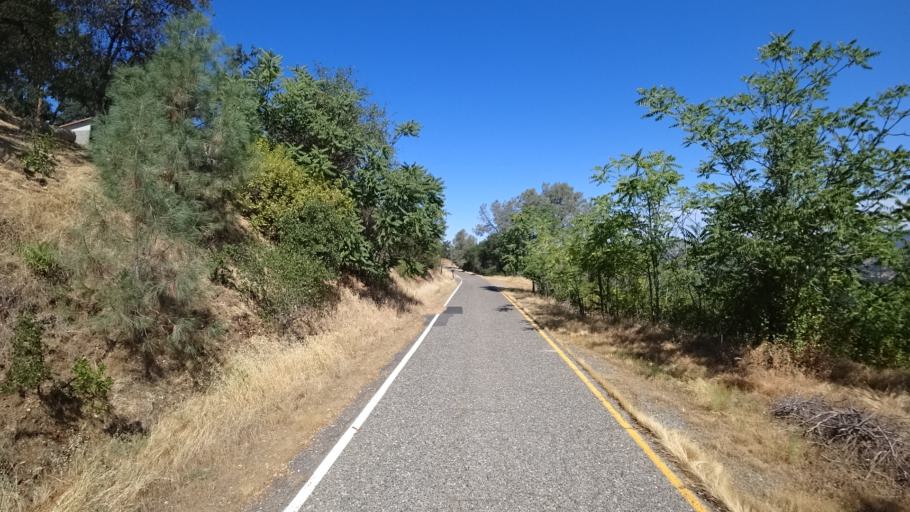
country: US
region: California
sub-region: Calaveras County
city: Copperopolis
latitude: 37.9300
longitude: -120.6320
